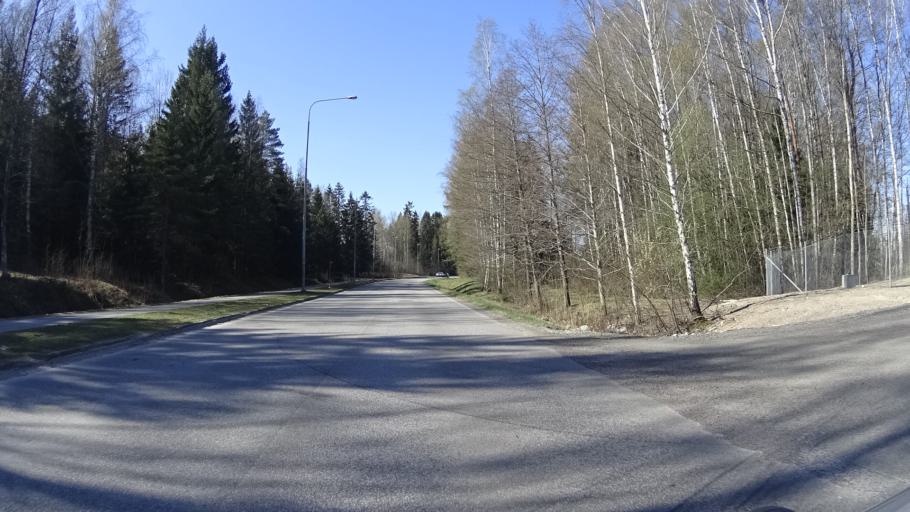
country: SE
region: Soedermanland
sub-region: Katrineholms Kommun
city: Katrineholm
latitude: 58.9918
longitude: 16.2358
